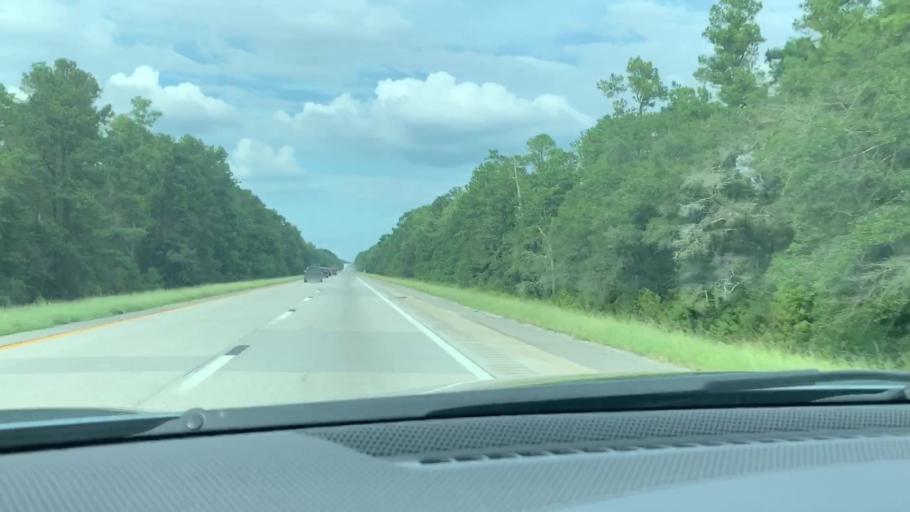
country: US
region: South Carolina
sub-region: Dorchester County
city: Saint George
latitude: 33.1039
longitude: -80.6444
